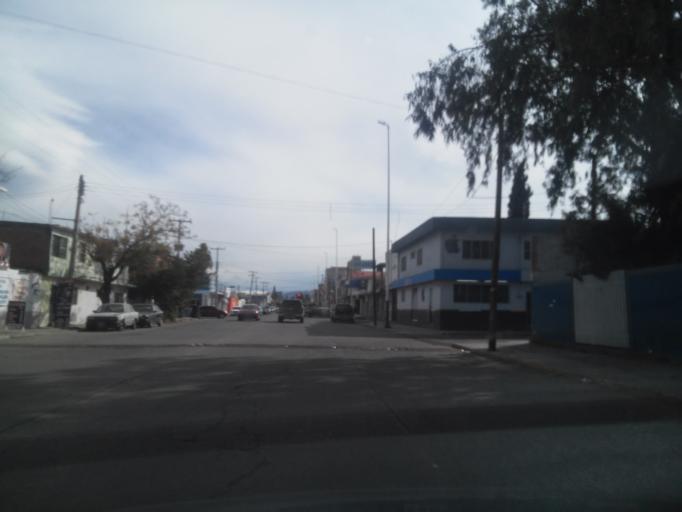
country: MX
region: Durango
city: Victoria de Durango
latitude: 24.0142
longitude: -104.6560
